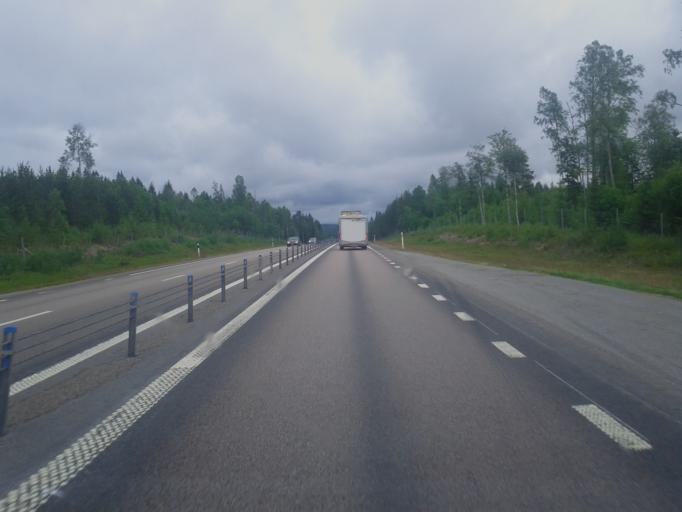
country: SE
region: Vaesternorrland
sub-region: Haernoesands Kommun
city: Haernoesand
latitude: 62.5689
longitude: 17.7388
